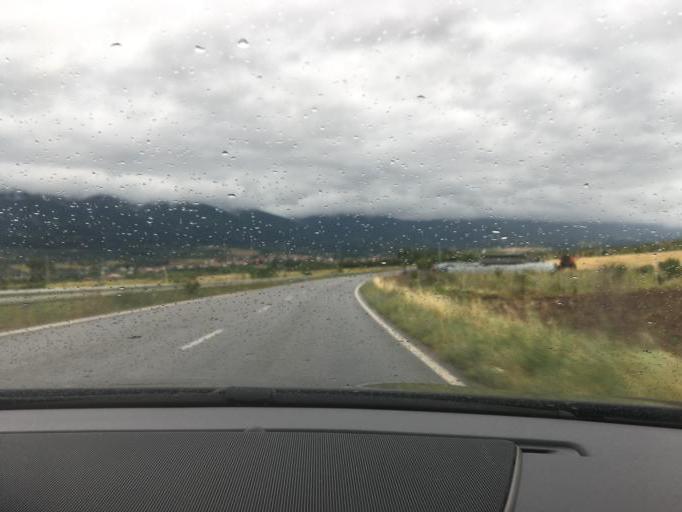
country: BG
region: Kyustendil
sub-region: Obshtina Kyustendil
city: Kyustendil
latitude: 42.2872
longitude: 22.6671
